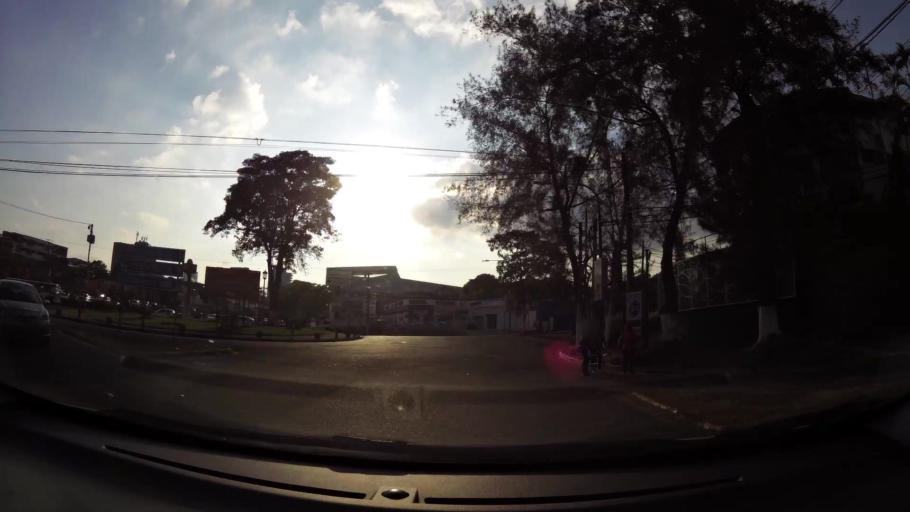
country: SV
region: La Libertad
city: Antiguo Cuscatlan
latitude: 13.6901
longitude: -89.2397
